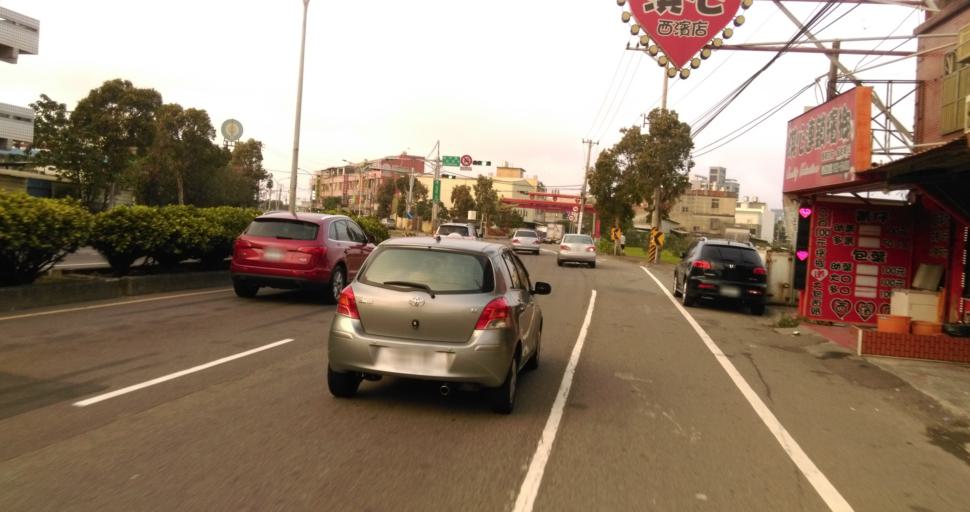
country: TW
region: Taiwan
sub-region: Hsinchu
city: Hsinchu
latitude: 24.8266
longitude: 120.9276
